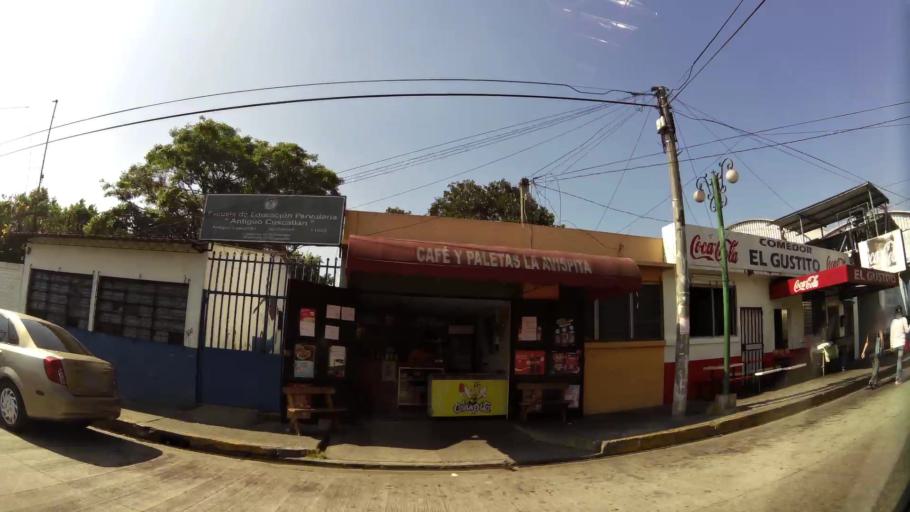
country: SV
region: La Libertad
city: Antiguo Cuscatlan
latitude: 13.6741
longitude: -89.2429
